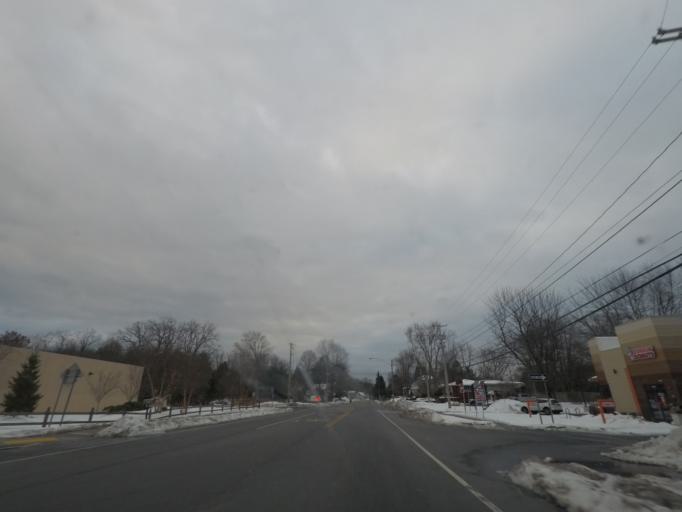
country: US
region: New York
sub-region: Ulster County
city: Plattekill
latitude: 41.6665
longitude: -74.1068
